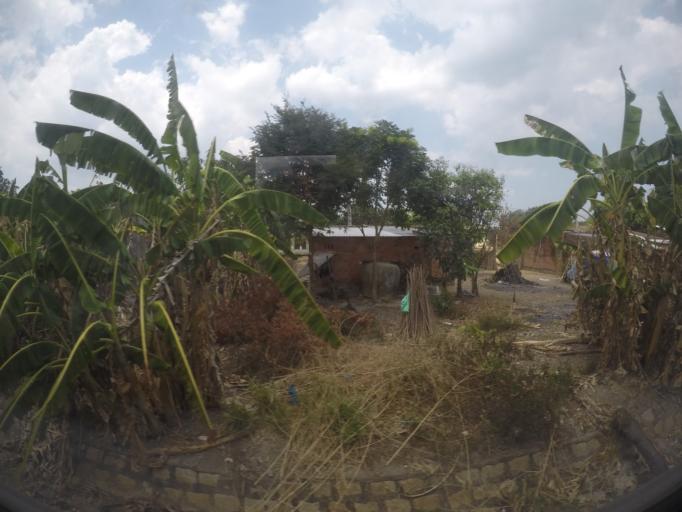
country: VN
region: Binh Thuan
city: Tanh Linh
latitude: 10.9286
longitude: 107.6656
